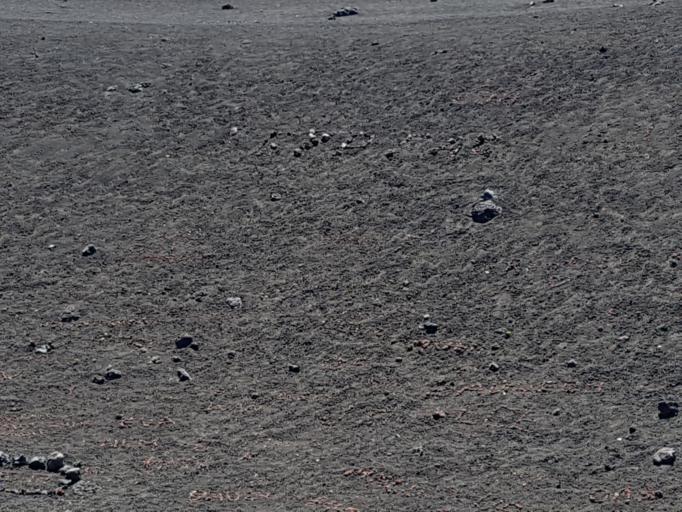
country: IT
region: Sicily
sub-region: Enna
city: Troina
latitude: 37.7875
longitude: 14.5944
